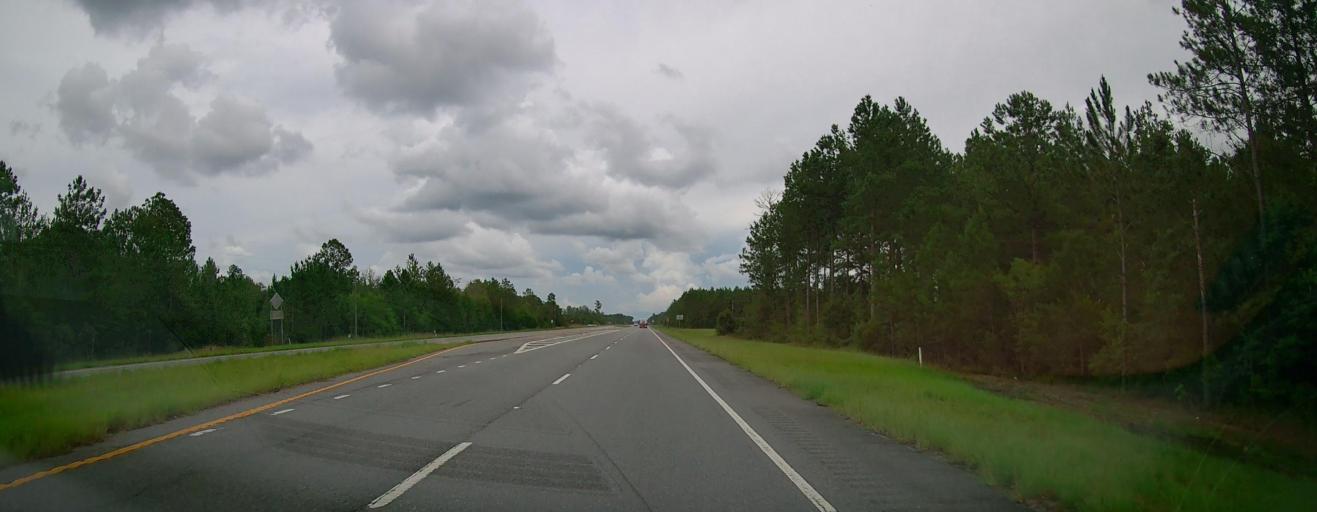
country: US
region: Georgia
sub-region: Wayne County
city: Jesup
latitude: 31.6774
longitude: -82.0803
